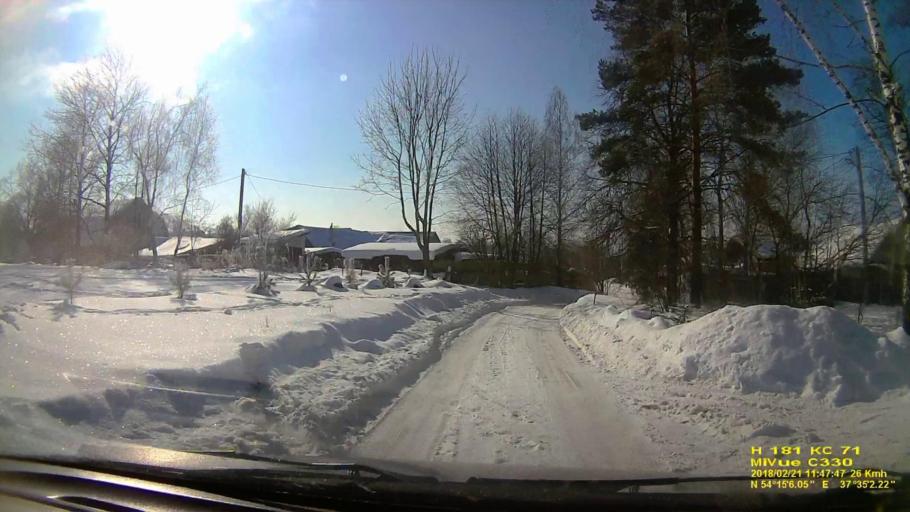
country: RU
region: Tula
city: Gorelki
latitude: 54.2516
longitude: 37.5842
